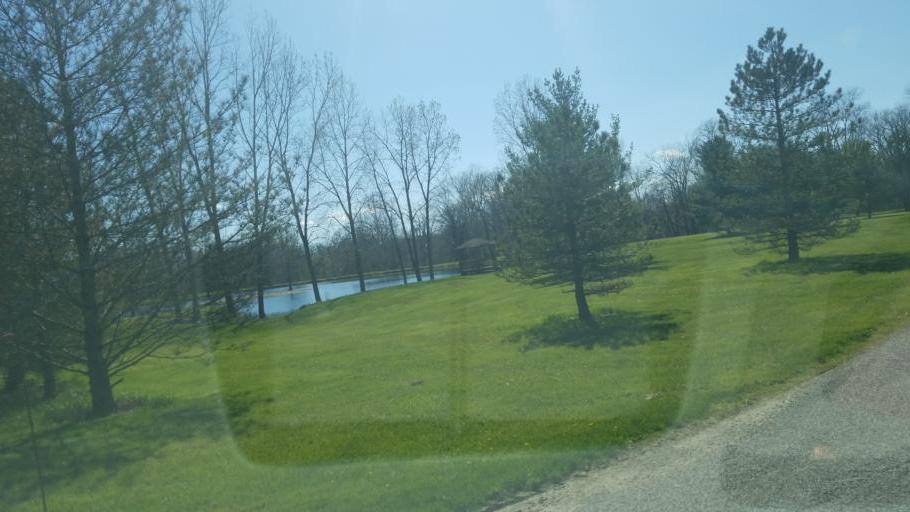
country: US
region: Ohio
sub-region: Delaware County
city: Ashley
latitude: 40.4680
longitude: -82.9476
